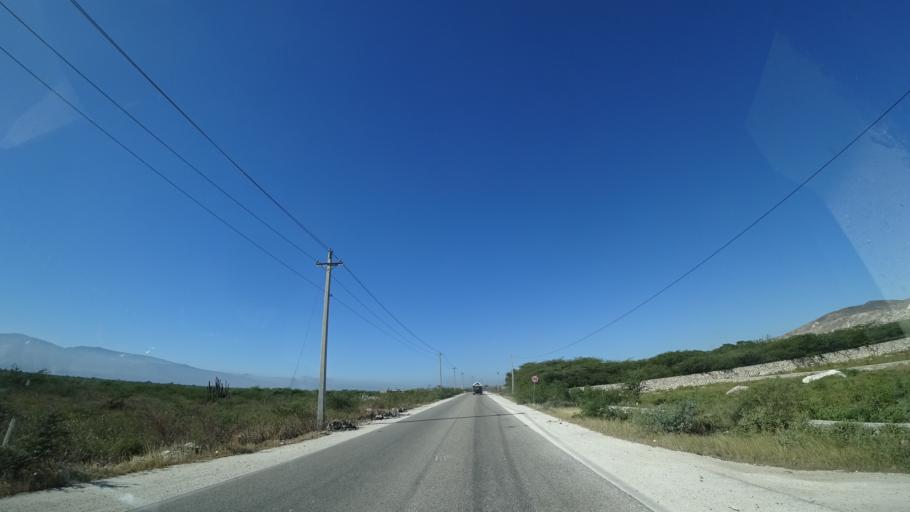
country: HT
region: Ouest
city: Croix des Bouquets
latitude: 18.6495
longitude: -72.2270
